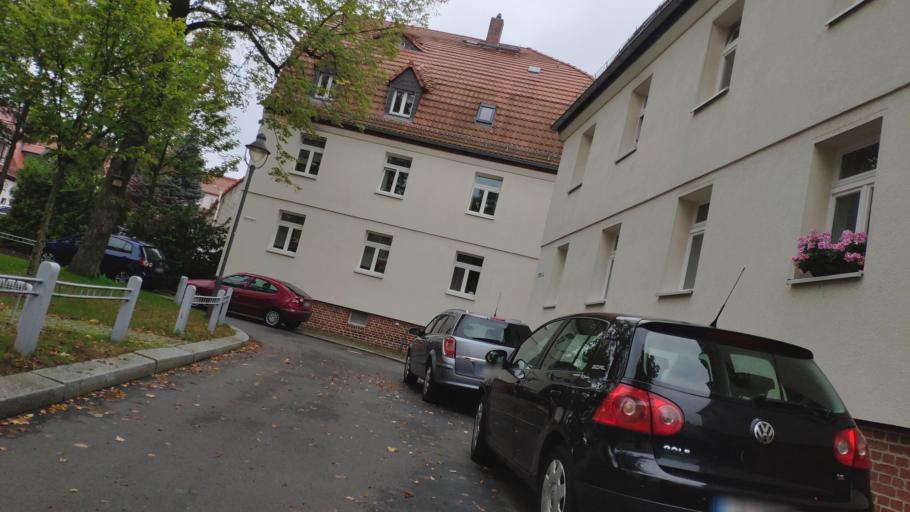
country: DE
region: Saxony
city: Chemnitz
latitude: 50.8236
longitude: 12.9545
